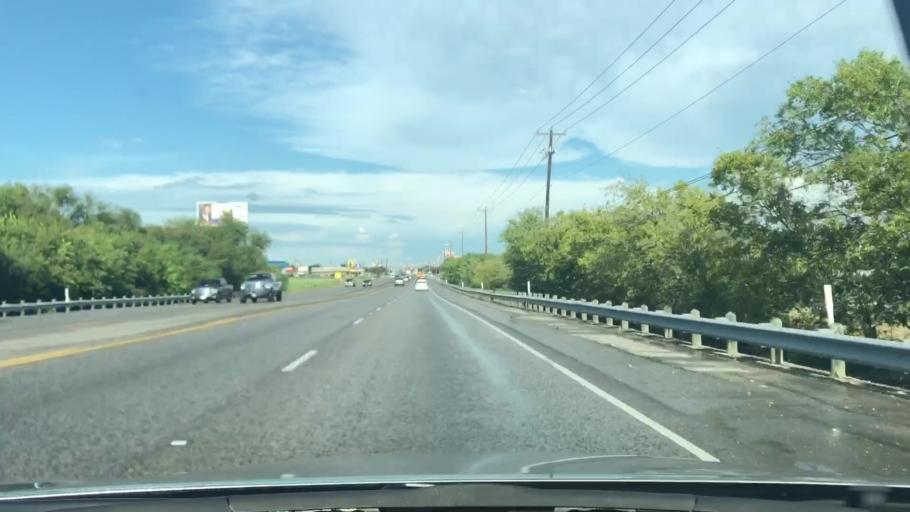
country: US
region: Texas
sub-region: Bexar County
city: Kirby
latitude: 29.4774
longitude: -98.3670
